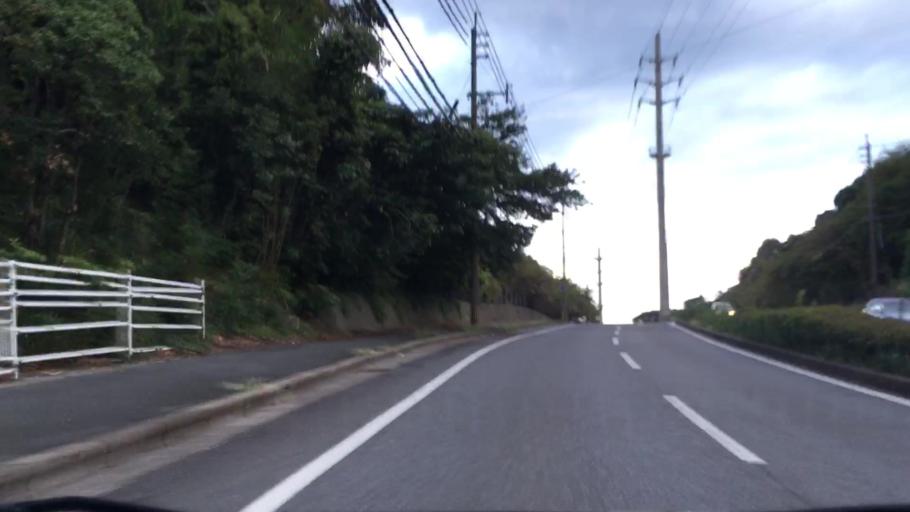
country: JP
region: Yamaguchi
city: Shimonoseki
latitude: 33.8877
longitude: 130.9806
